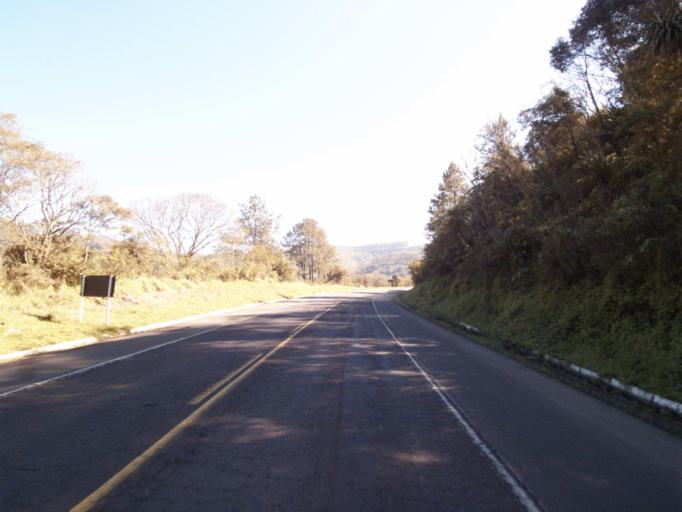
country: BR
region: Rio Grande do Sul
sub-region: Frederico Westphalen
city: Frederico Westphalen
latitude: -27.0335
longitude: -53.2339
